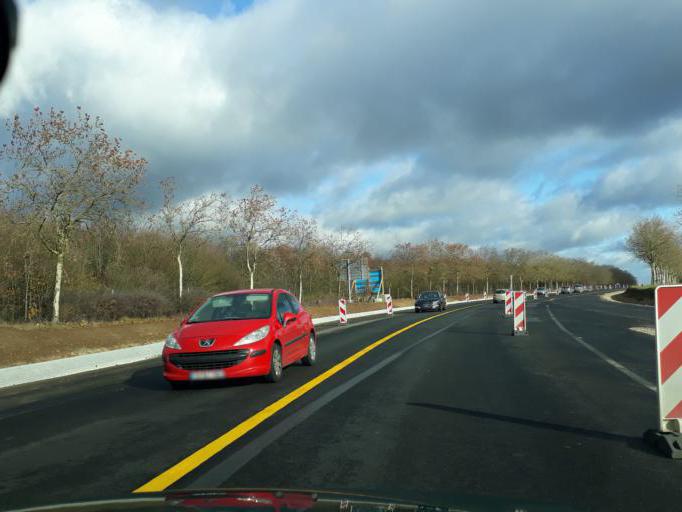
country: FR
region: Centre
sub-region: Departement du Loir-et-Cher
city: Villebarou
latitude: 47.6119
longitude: 1.3400
